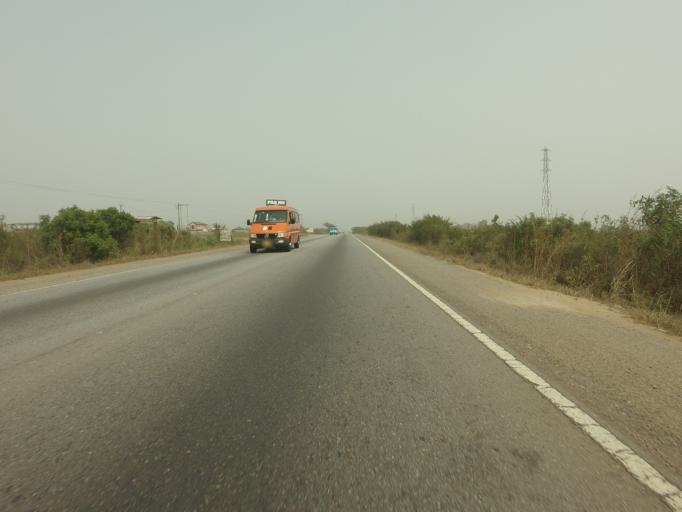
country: GH
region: Greater Accra
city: Tema
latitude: 5.7918
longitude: 0.1184
